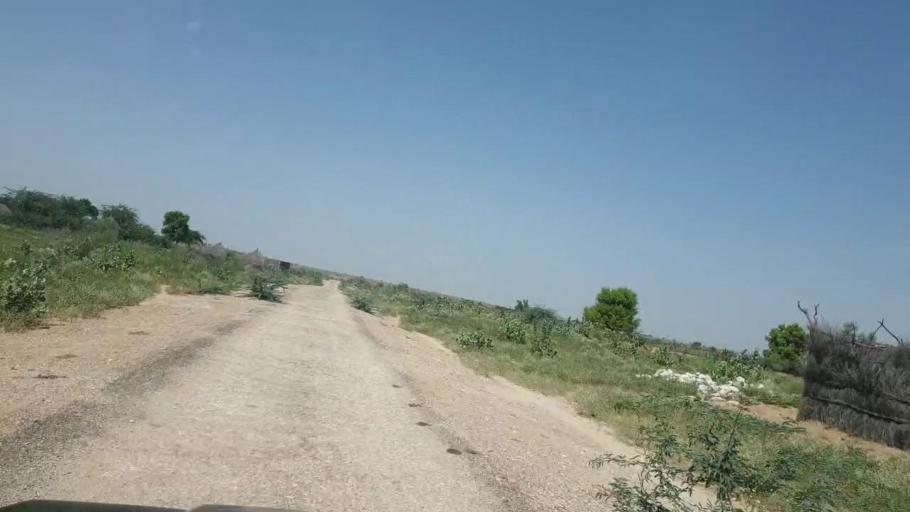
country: PK
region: Sindh
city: Chor
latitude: 25.3682
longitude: 70.3209
